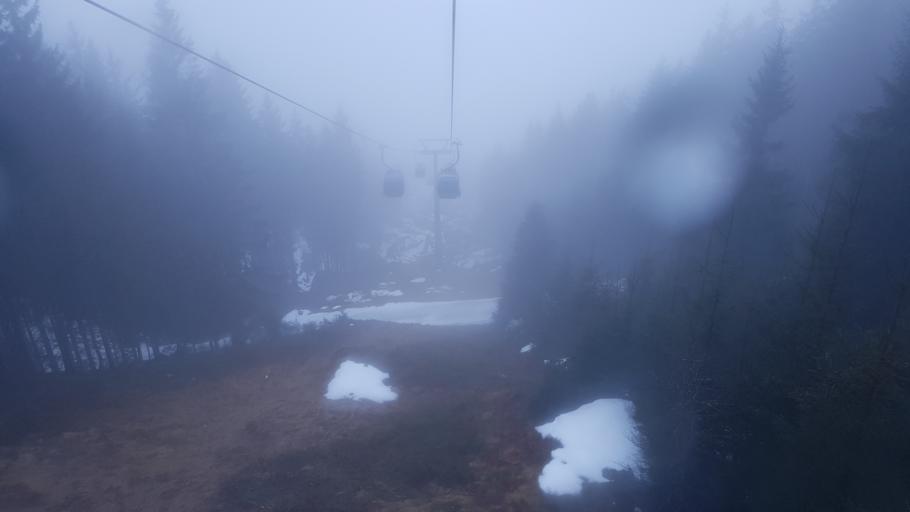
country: AT
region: Salzburg
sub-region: Politischer Bezirk Zell am See
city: Neukirchen am Grossvenediger
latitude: 47.2641
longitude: 12.2806
